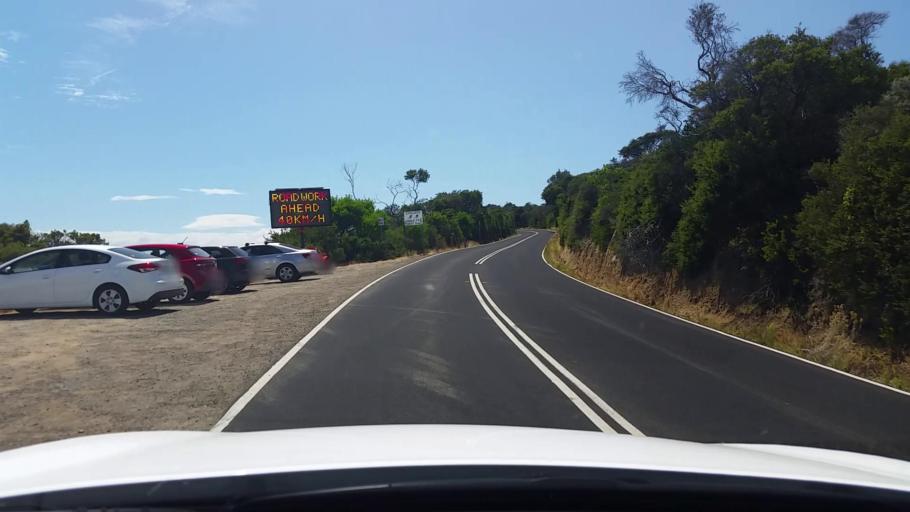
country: AU
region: Victoria
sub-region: Mornington Peninsula
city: Mount Martha
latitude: -38.2808
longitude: 144.9967
